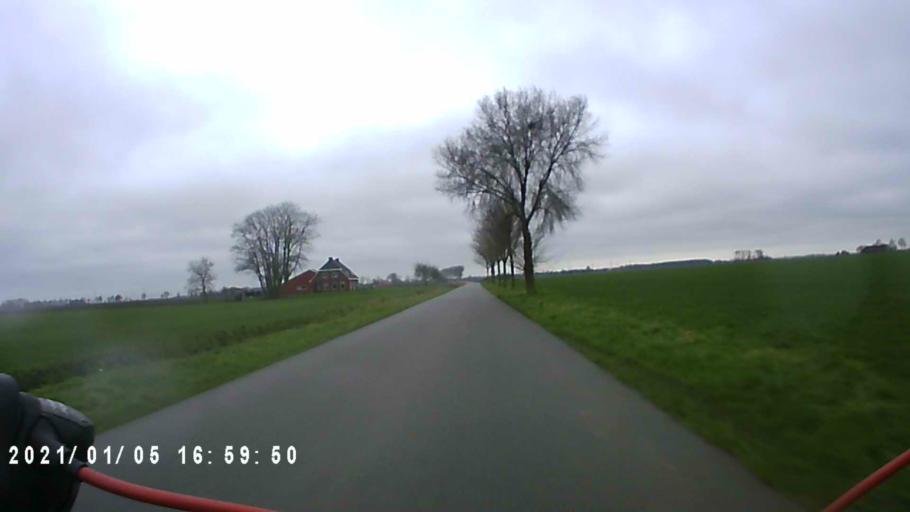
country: NL
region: Groningen
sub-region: Gemeente  Oldambt
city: Winschoten
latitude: 53.2528
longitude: 7.0504
